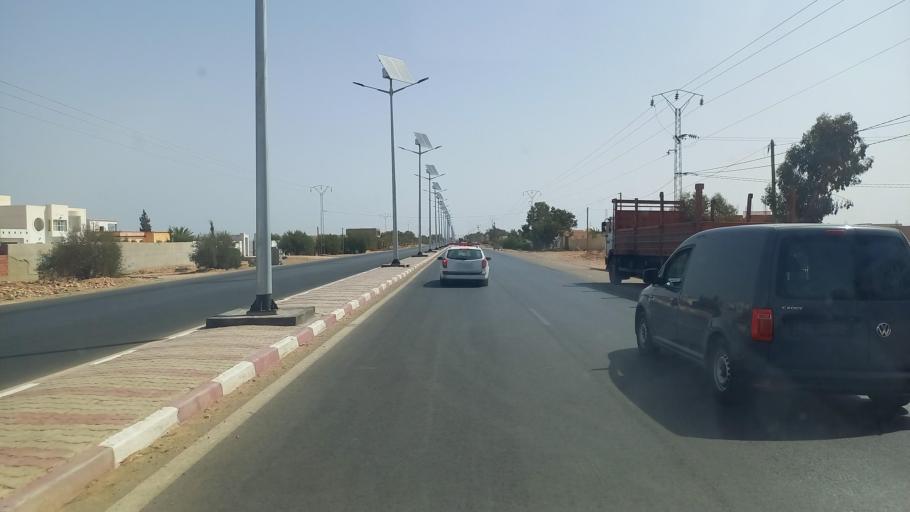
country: TN
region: Madanin
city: Medenine
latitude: 33.3547
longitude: 10.5406
